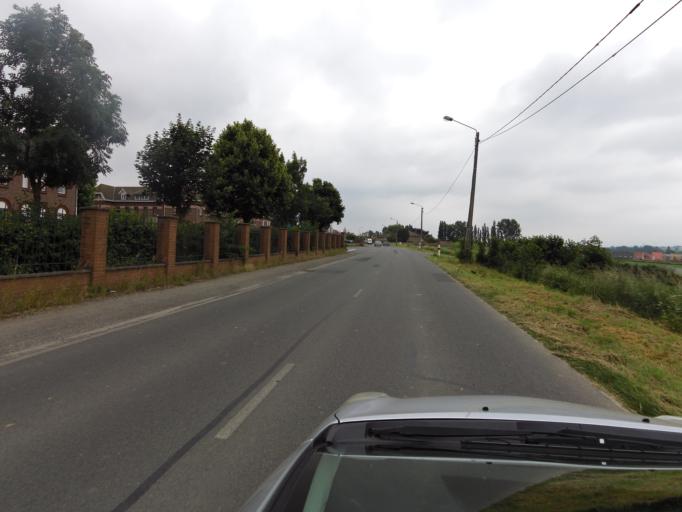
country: FR
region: Nord-Pas-de-Calais
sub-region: Departement du Nord
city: Bailleul
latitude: 50.7485
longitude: 2.7416
